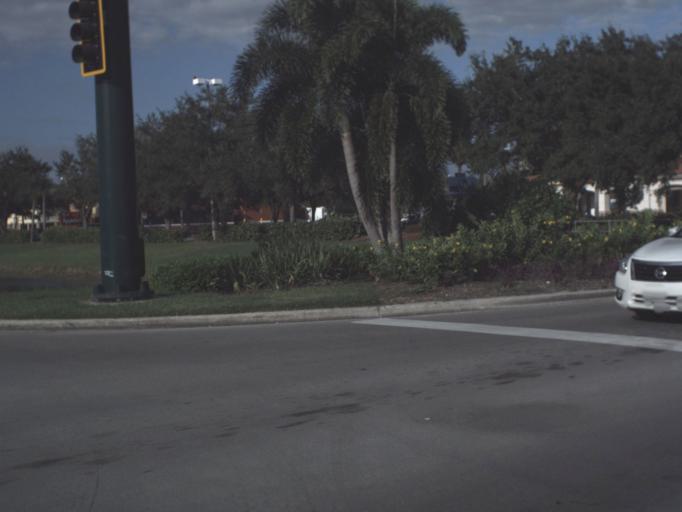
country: US
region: Florida
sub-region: Collier County
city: Pine Ridge
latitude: 26.2089
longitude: -81.7683
